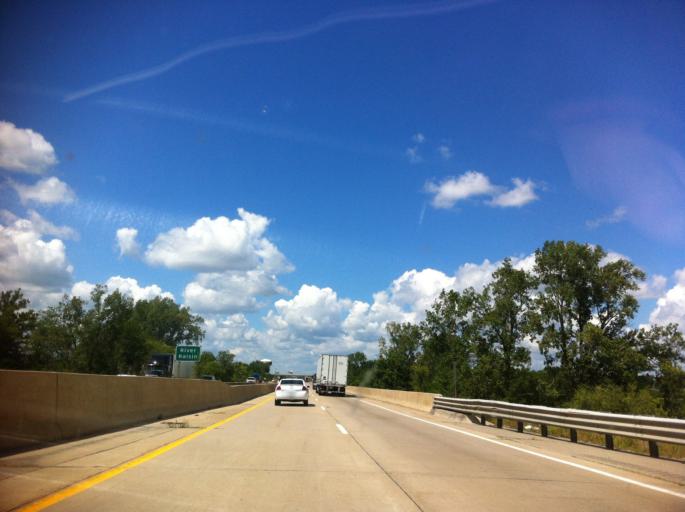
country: US
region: Michigan
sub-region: Monroe County
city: Dundee
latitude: 41.9451
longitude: -83.6654
